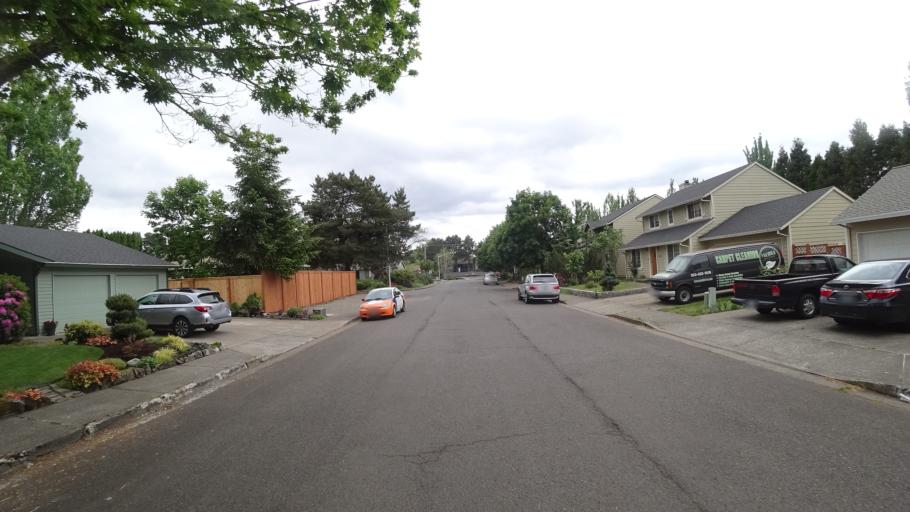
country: US
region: Oregon
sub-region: Washington County
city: Rockcreek
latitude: 45.5279
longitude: -122.8651
